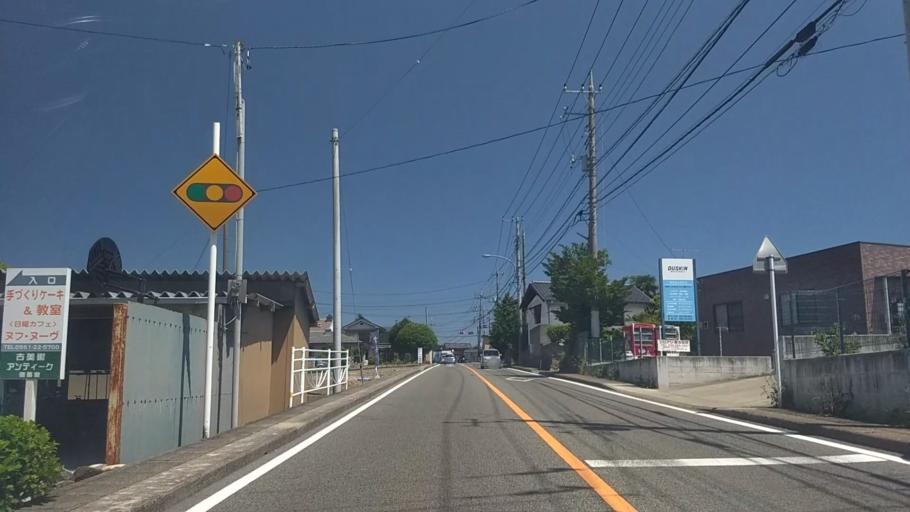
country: JP
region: Yamanashi
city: Nirasaki
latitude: 35.6769
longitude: 138.4649
